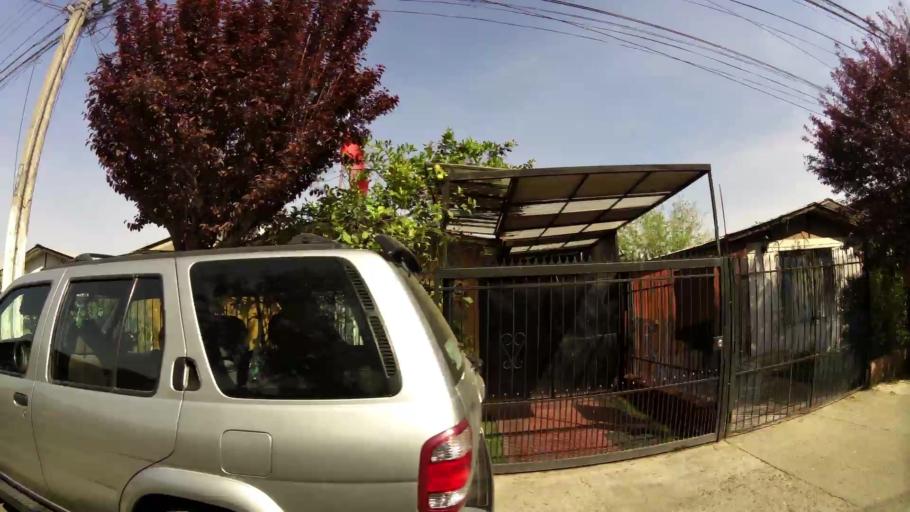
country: CL
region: Santiago Metropolitan
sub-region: Provincia de Santiago
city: Villa Presidente Frei, Nunoa, Santiago, Chile
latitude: -33.5250
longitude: -70.5588
